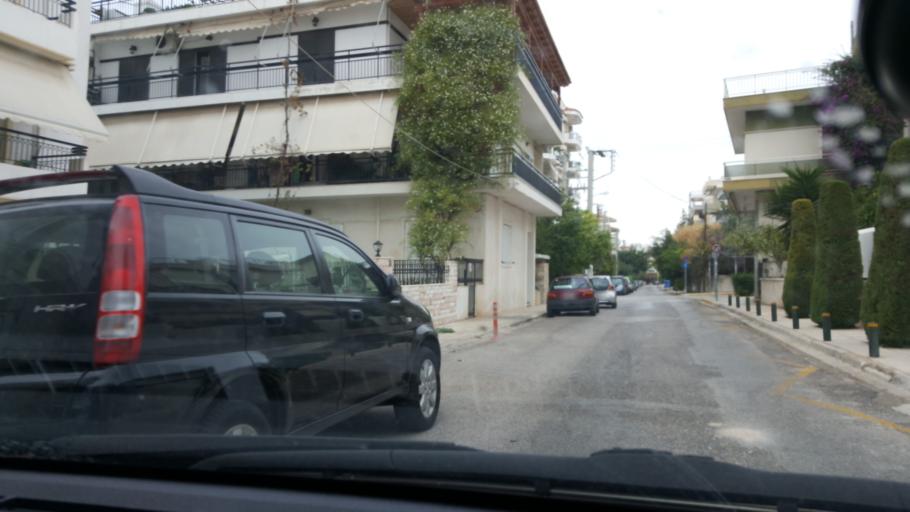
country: GR
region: Attica
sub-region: Nomarchia Athinas
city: Argyroupoli
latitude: 37.8931
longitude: 23.7501
